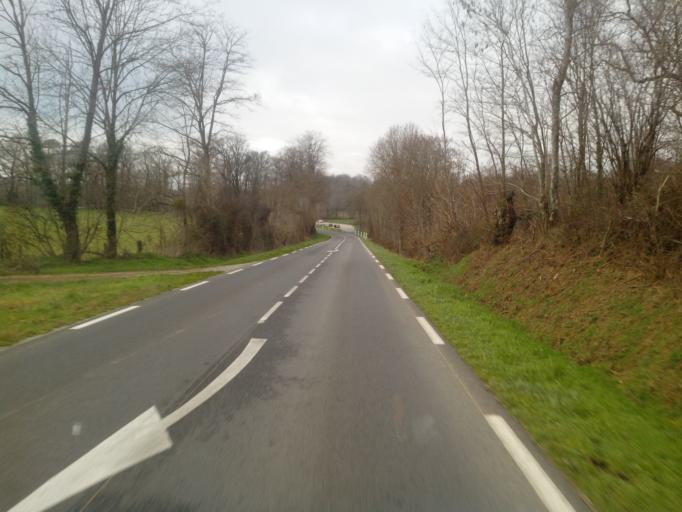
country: FR
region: Limousin
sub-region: Departement de la Haute-Vienne
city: Magnac-Laval
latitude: 46.2142
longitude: 1.1436
